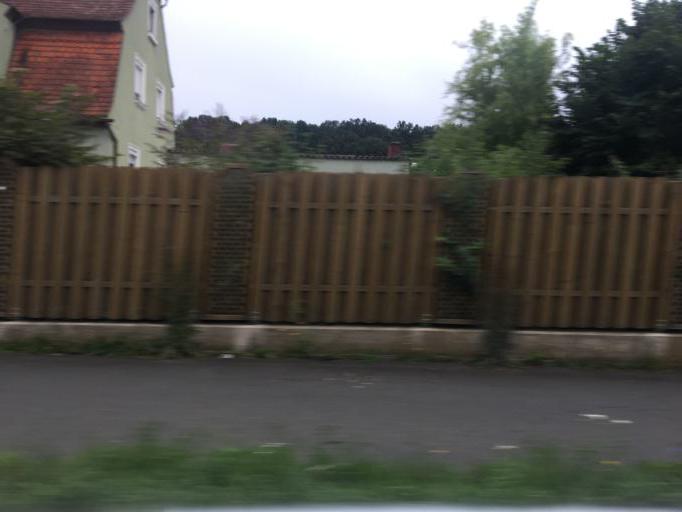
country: DE
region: Bavaria
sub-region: Regierungsbezirk Mittelfranken
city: Wilhermsdorf
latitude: 49.4894
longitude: 10.7449
